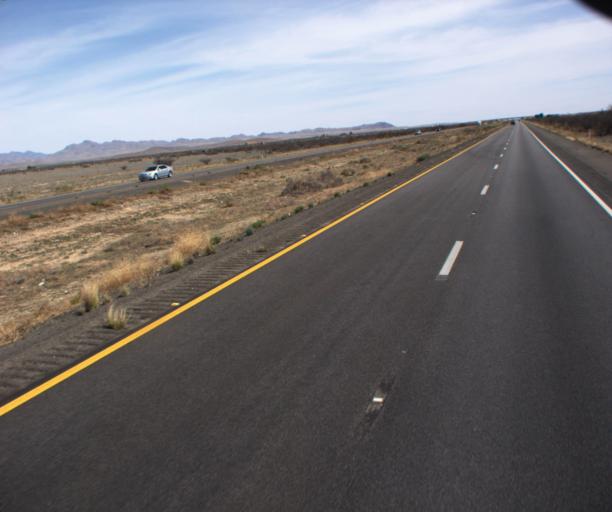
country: US
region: Arizona
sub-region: Cochise County
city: Willcox
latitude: 32.2940
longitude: -109.8134
